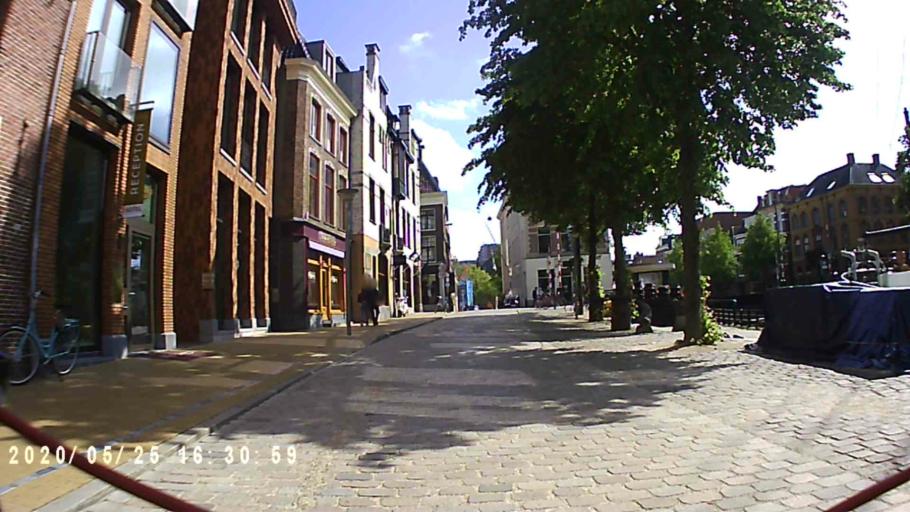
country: NL
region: Groningen
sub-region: Gemeente Groningen
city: Groningen
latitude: 53.2173
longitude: 6.5597
